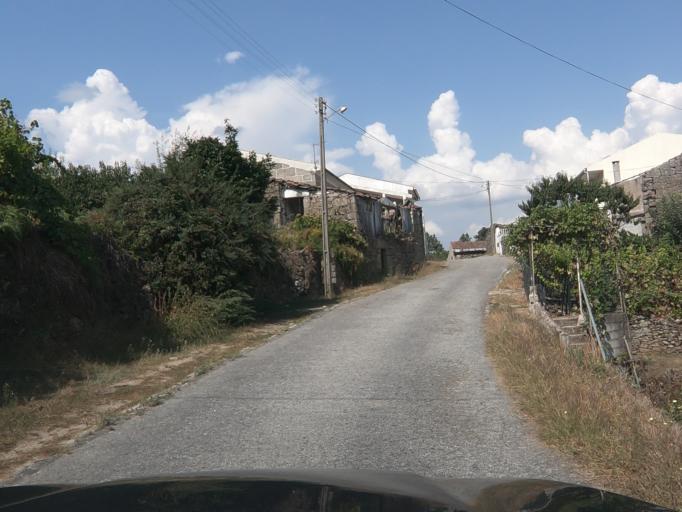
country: PT
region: Vila Real
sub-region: Sabrosa
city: Sabrosa
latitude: 41.3029
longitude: -7.5942
